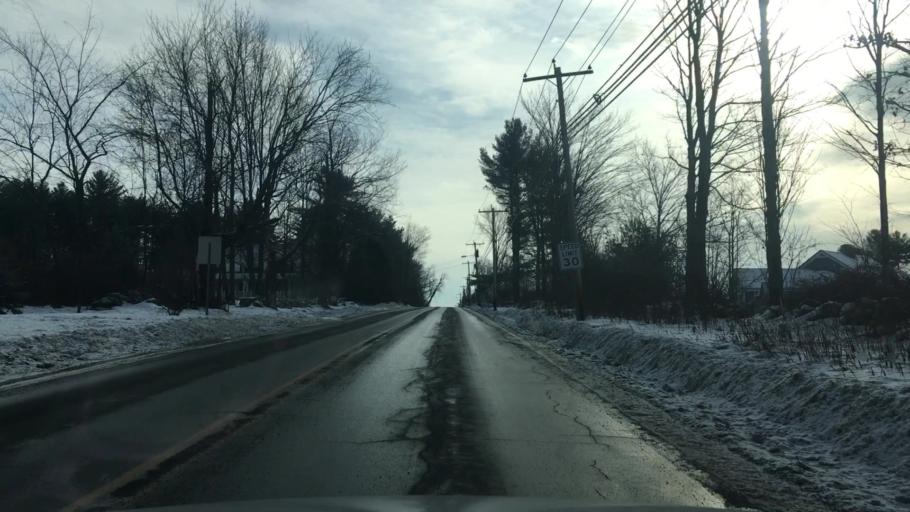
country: US
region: New Hampshire
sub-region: Grafton County
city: Enfield
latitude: 43.6299
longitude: -72.1302
